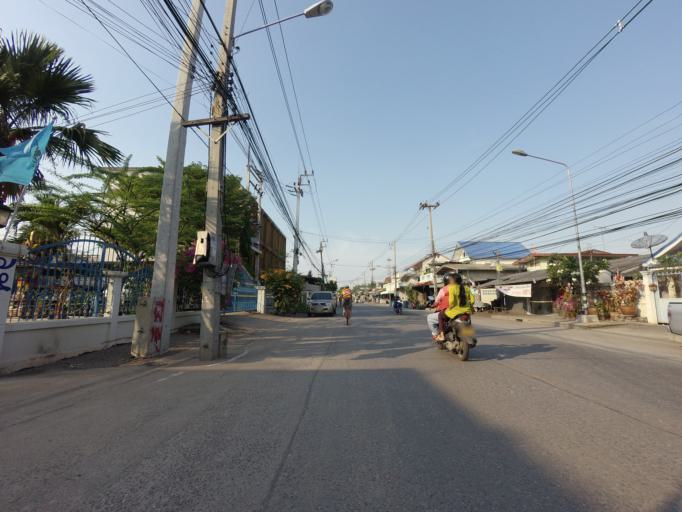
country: TH
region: Samut Sakhon
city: Samut Sakhon
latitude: 13.5379
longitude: 100.2799
